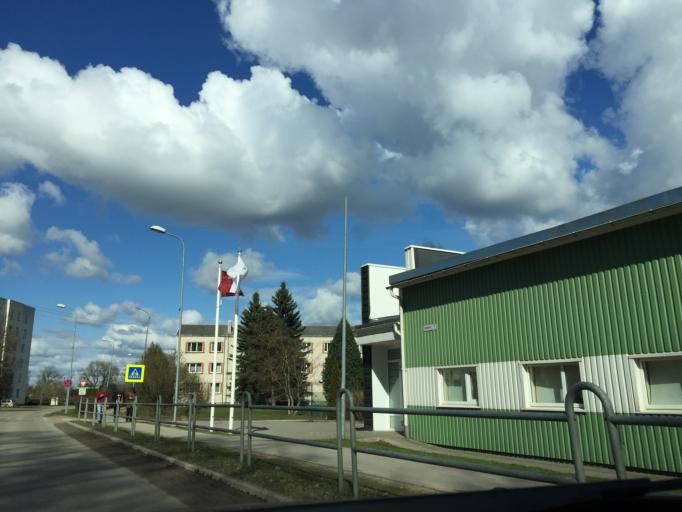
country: LV
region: Kekava
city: Kekava
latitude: 56.8294
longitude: 24.2317
